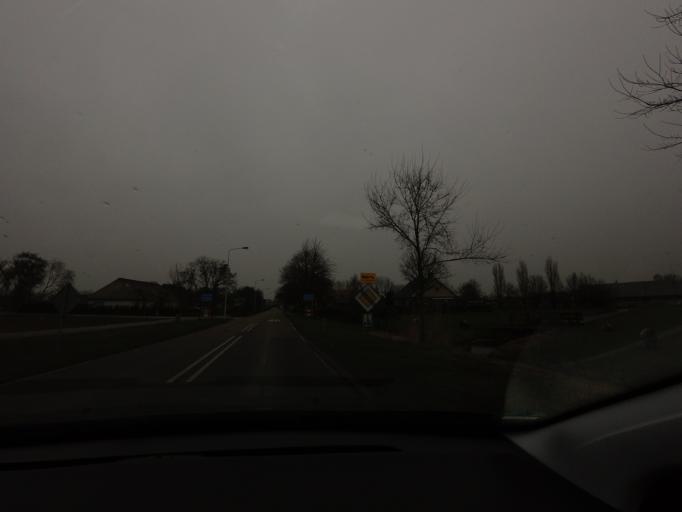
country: NL
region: Friesland
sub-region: Gemeente Franekeradeel
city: Franeker
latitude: 53.1807
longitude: 5.5550
